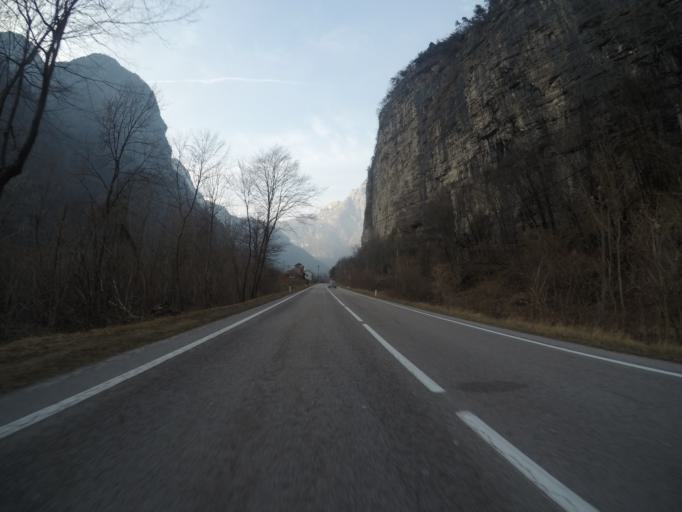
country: IT
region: Veneto
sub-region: Provincia di Belluno
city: La Valle Agordina
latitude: 46.2291
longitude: 12.1148
